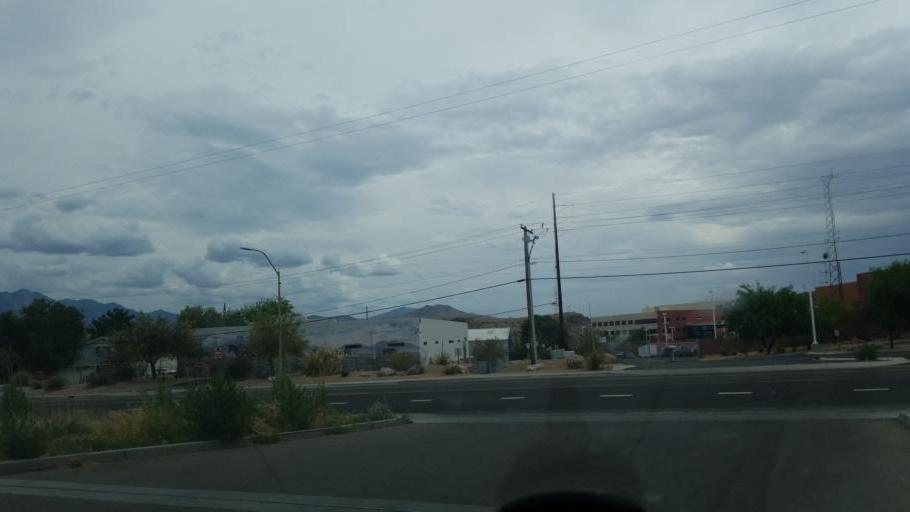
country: US
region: Arizona
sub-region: Mohave County
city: Kingman
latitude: 35.1909
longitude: -114.0641
